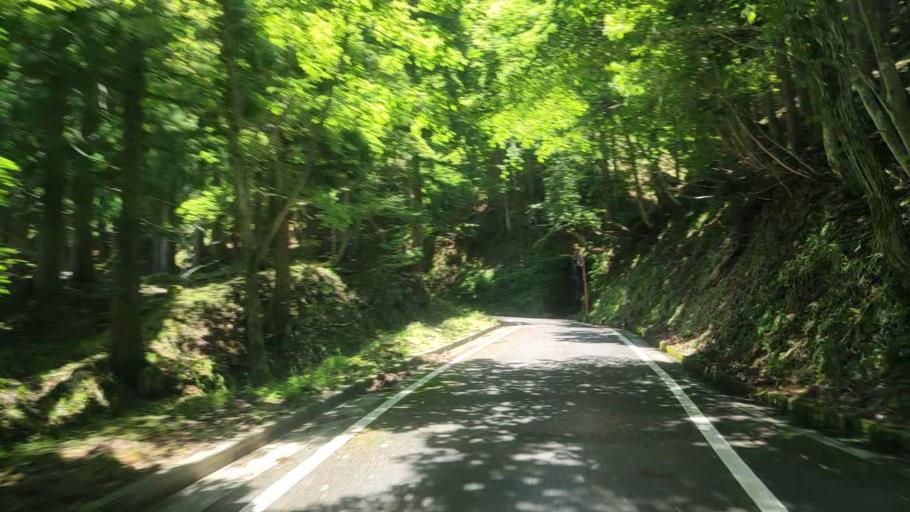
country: JP
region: Tottori
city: Tottori
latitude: 35.3787
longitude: 134.4902
